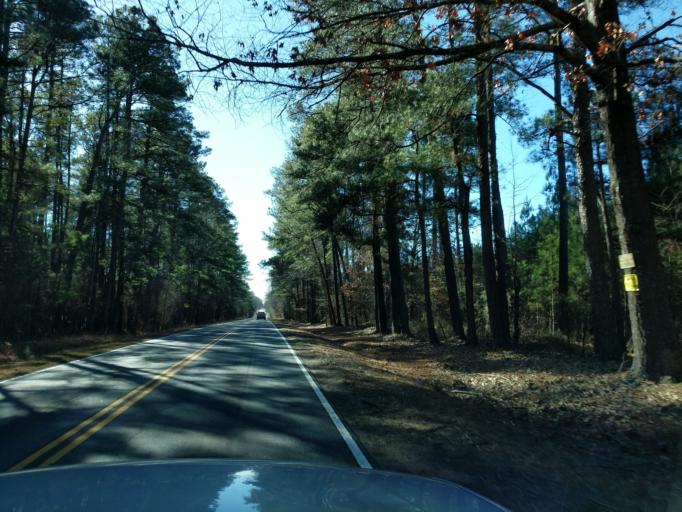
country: US
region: South Carolina
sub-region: Greenwood County
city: Ninety Six
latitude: 34.2449
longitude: -81.8696
